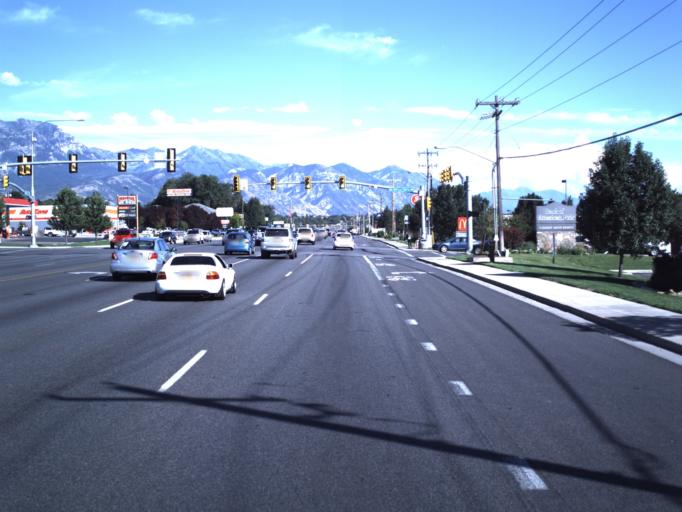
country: US
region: Utah
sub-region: Utah County
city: Pleasant Grove
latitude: 40.3560
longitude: -111.7367
